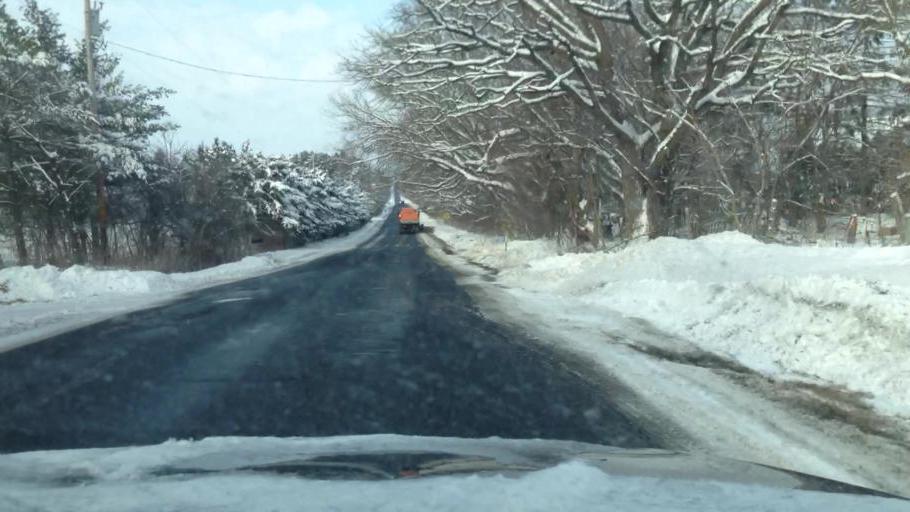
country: US
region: Wisconsin
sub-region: Walworth County
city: East Troy
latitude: 42.7599
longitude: -88.4456
